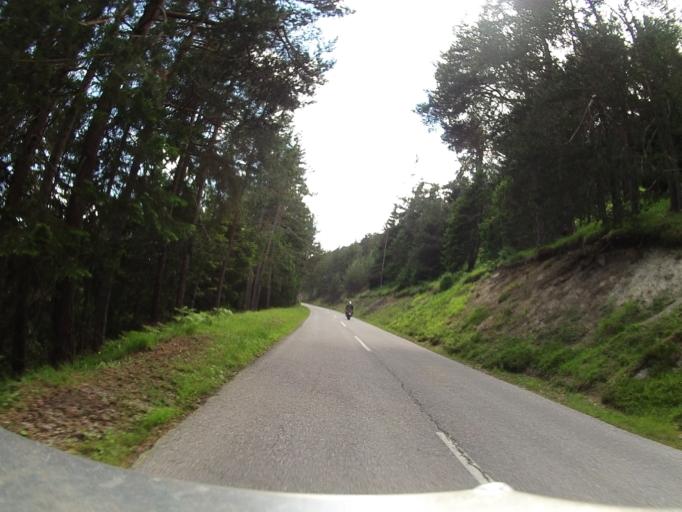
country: AT
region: Tyrol
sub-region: Politischer Bezirk Imst
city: Tarrenz
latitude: 47.2795
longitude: 10.7407
